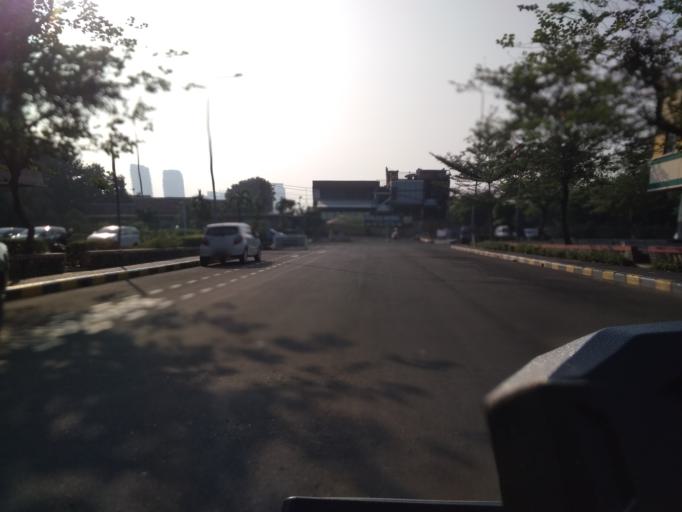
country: ID
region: Jakarta Raya
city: Jakarta
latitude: -6.2640
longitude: 106.7997
